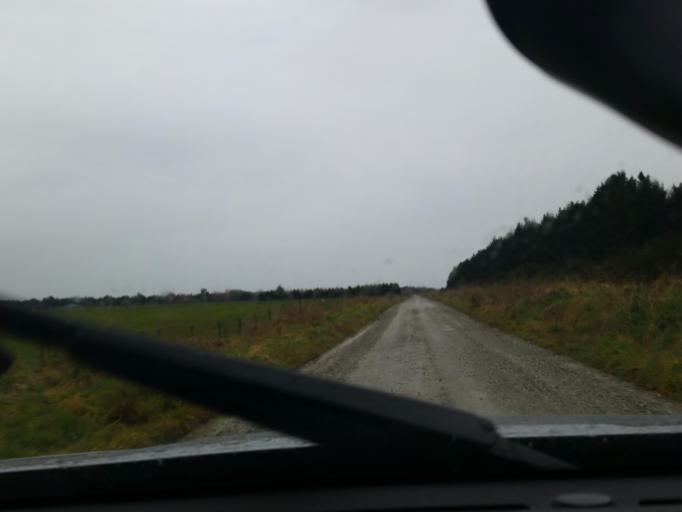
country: NZ
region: Southland
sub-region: Southland District
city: Winton
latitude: -46.2344
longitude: 168.4835
